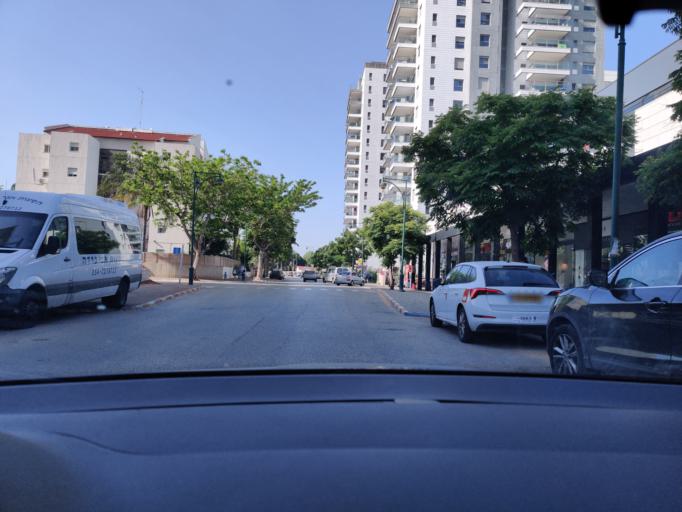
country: IL
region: Haifa
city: Hadera
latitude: 32.4677
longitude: 34.9528
